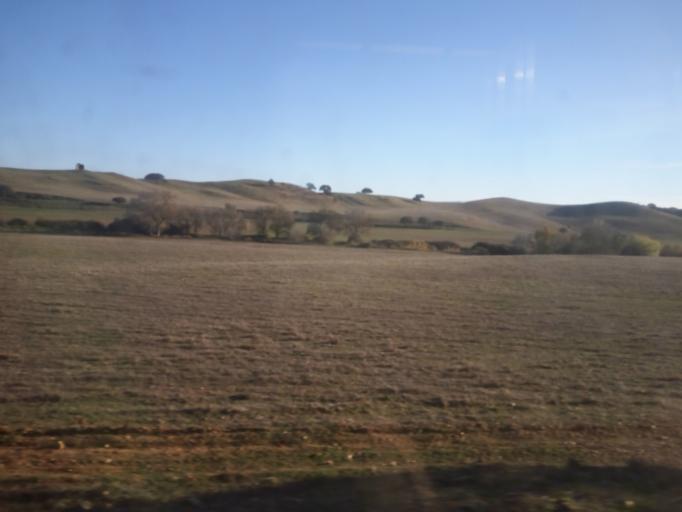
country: PT
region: Beja
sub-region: Ourique
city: Ourique
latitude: 37.7088
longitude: -8.3513
